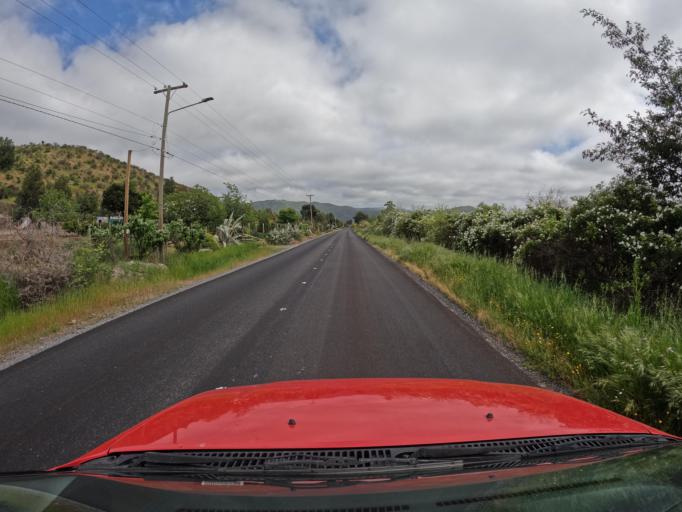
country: CL
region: O'Higgins
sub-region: Provincia de Colchagua
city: Santa Cruz
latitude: -34.6610
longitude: -71.4006
